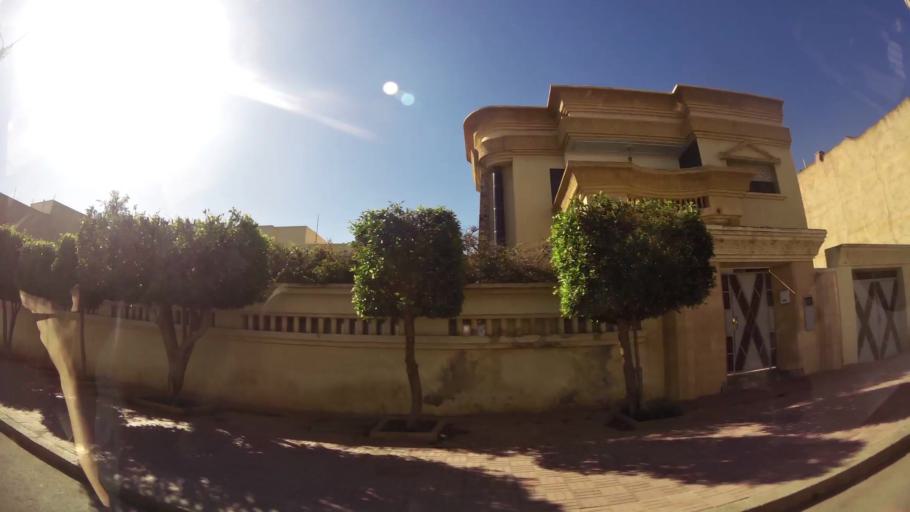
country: MA
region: Oriental
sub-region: Oujda-Angad
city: Oujda
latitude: 34.6550
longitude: -1.8928
